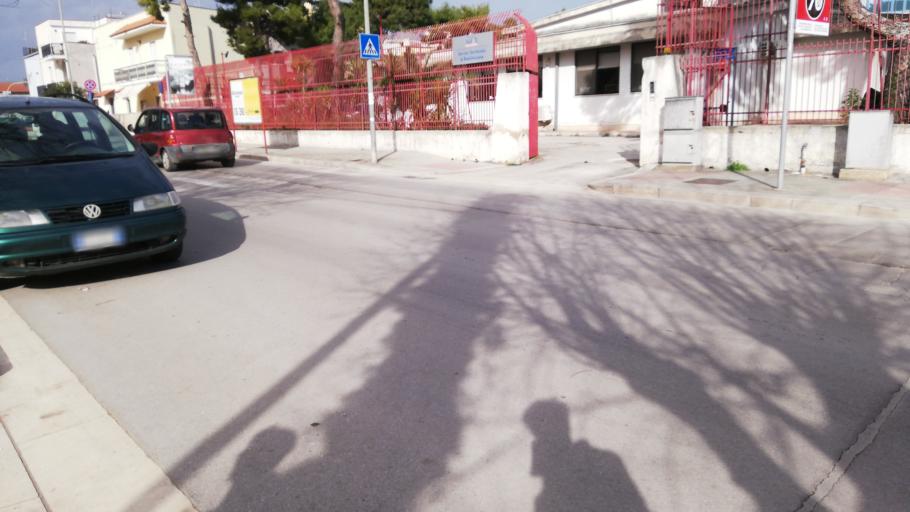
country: IT
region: Apulia
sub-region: Provincia di Barletta - Andria - Trani
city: Andria
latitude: 41.2399
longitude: 16.2954
